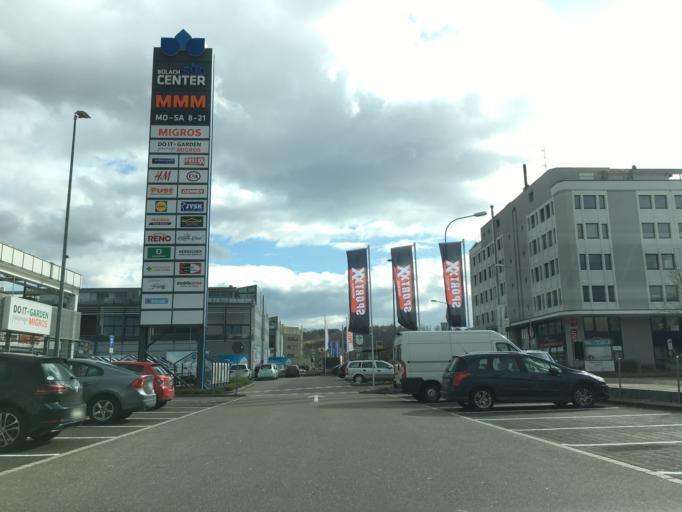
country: CH
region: Zurich
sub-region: Bezirk Buelach
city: Buelach / Niederflachs
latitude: 47.5096
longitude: 8.5391
